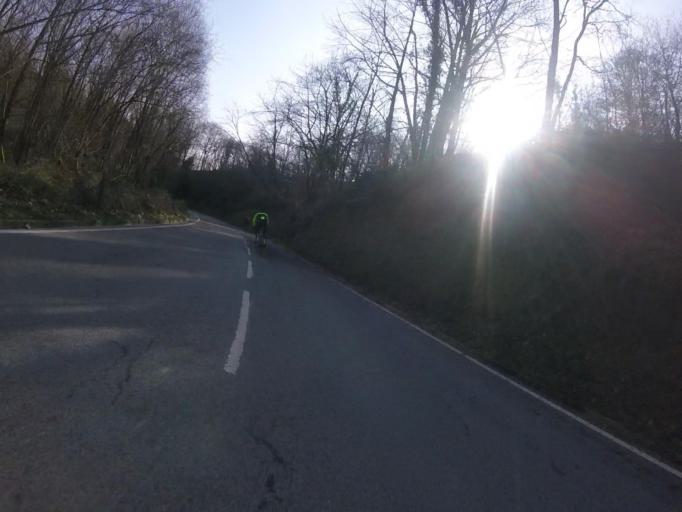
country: ES
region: Navarre
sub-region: Provincia de Navarra
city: Bera
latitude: 43.2913
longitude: -1.6867
